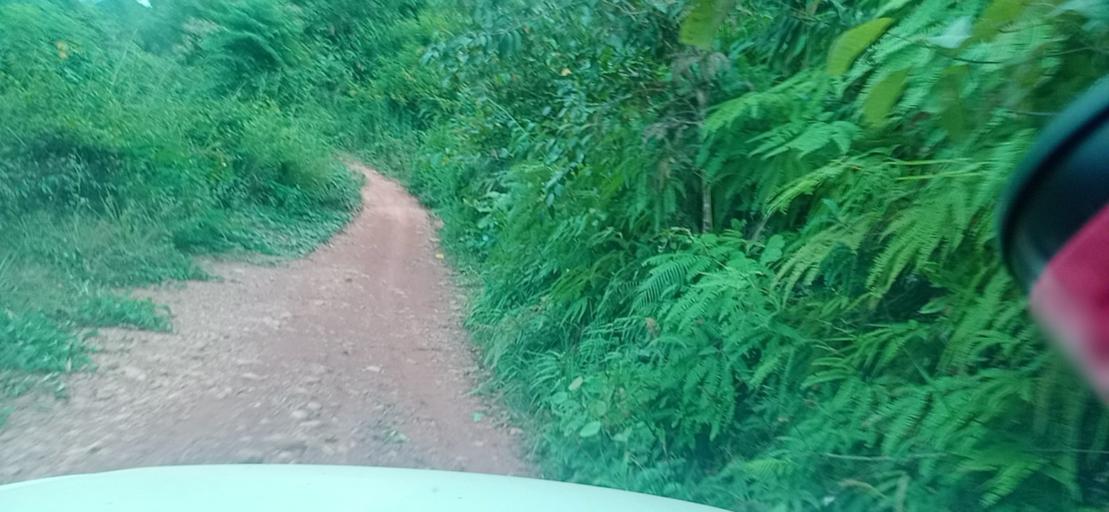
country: TH
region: Changwat Bueng Kan
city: Pak Khat
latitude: 18.5599
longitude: 103.2937
